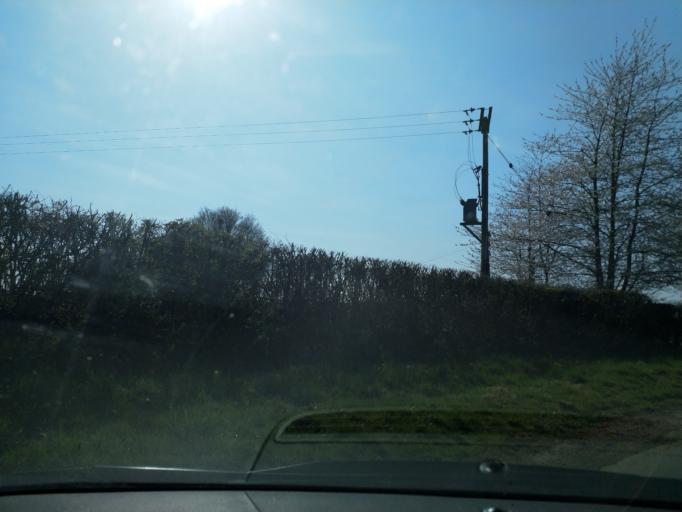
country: GB
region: England
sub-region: Warwickshire
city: Wroxall
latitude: 52.2940
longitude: -1.6894
